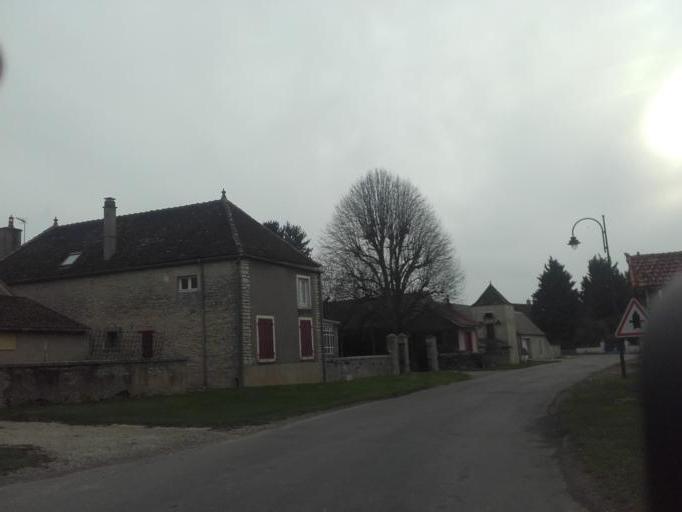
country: FR
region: Bourgogne
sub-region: Departement de Saone-et-Loire
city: Gergy
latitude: 46.9905
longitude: 4.9465
